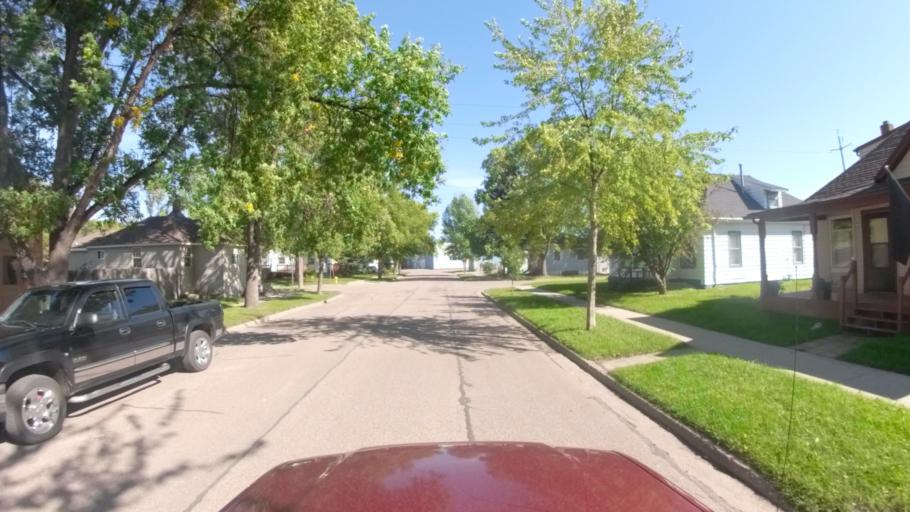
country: US
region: North Dakota
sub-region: Grand Forks County
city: Grand Forks
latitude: 47.9232
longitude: -97.0425
